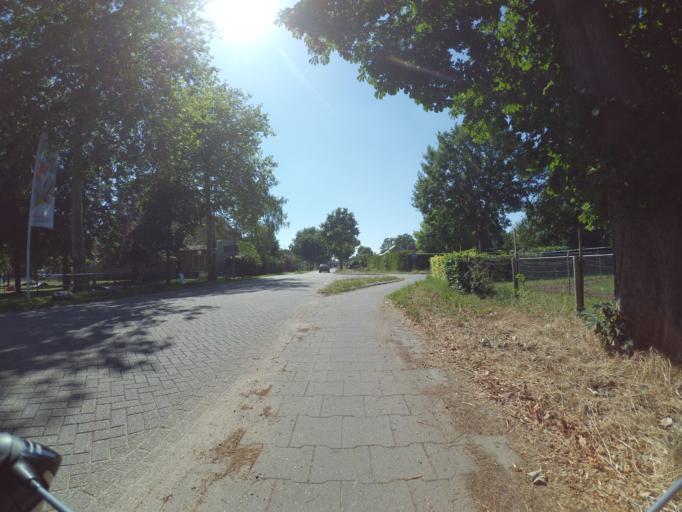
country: NL
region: North Brabant
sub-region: Gemeente Waalwijk
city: Waalwijk
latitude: 51.6616
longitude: 5.0624
